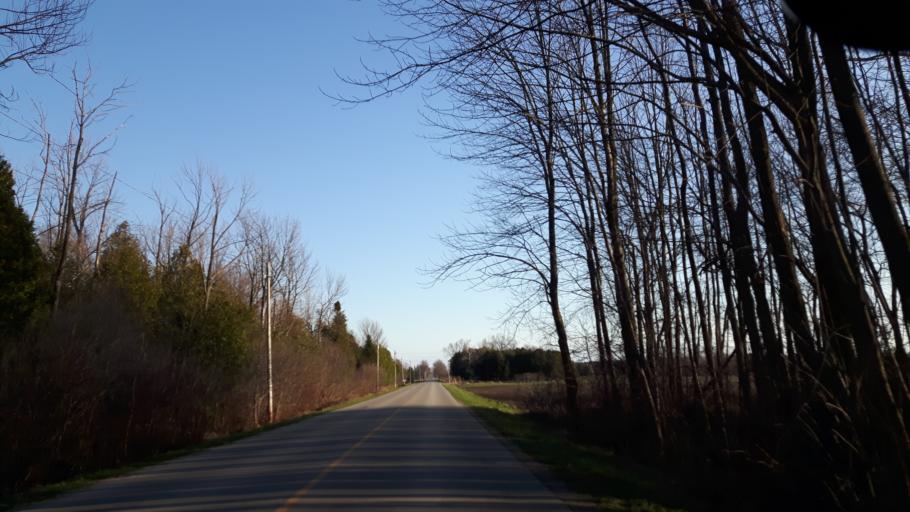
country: CA
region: Ontario
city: Goderich
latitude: 43.6877
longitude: -81.6848
